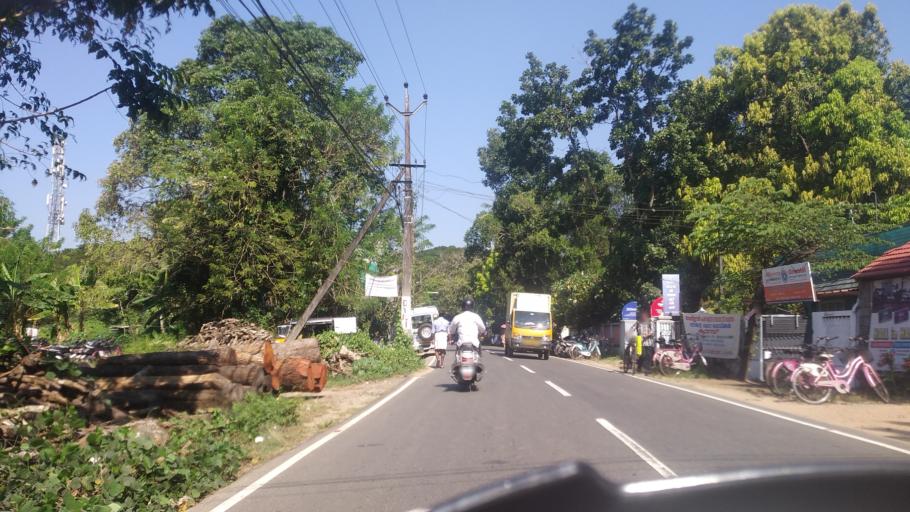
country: IN
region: Kerala
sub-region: Ernakulam
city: Elur
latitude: 10.1216
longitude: 76.2460
